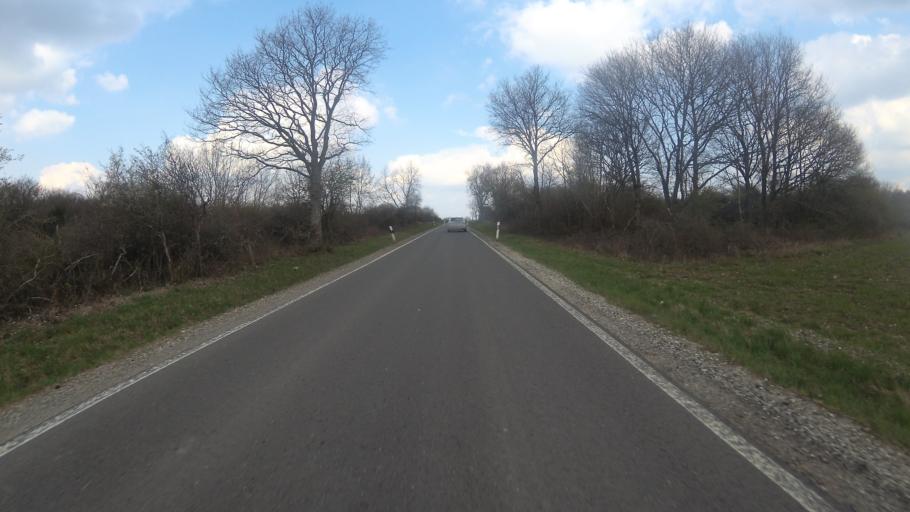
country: DE
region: Rheinland-Pfalz
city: Polich
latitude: 49.7696
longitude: 6.8475
